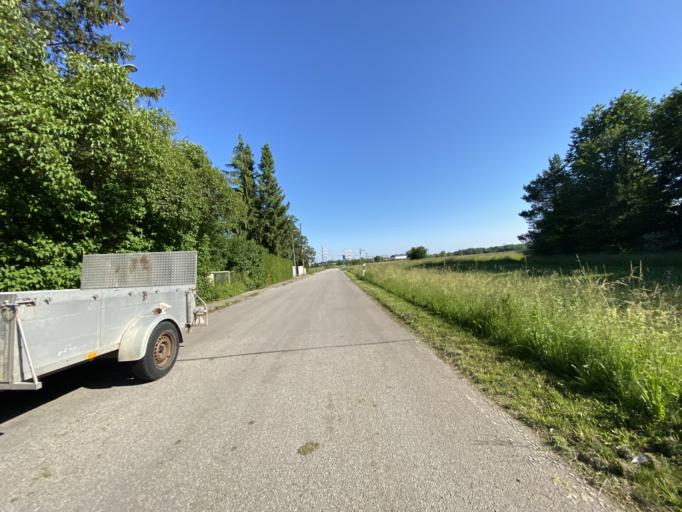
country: DE
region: Bavaria
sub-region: Upper Bavaria
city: Pasing
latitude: 48.1663
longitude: 11.4418
